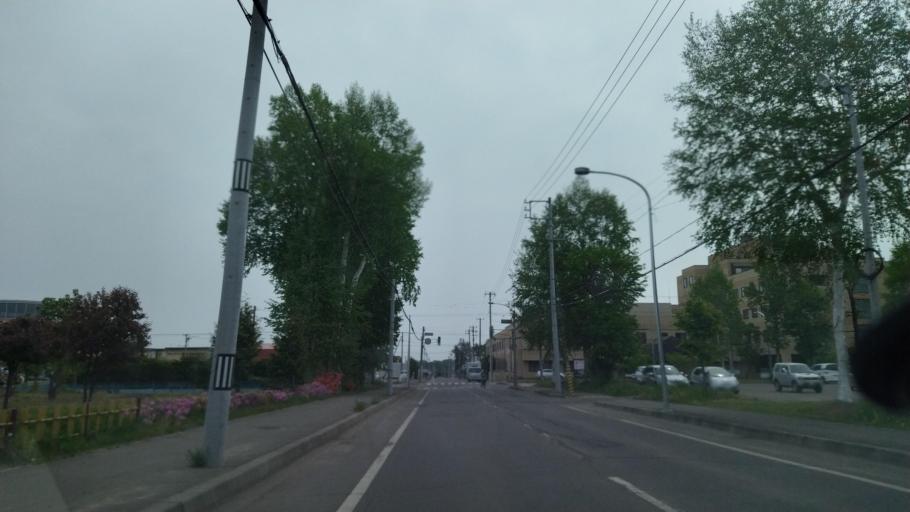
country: JP
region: Hokkaido
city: Obihiro
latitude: 42.9134
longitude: 143.0530
